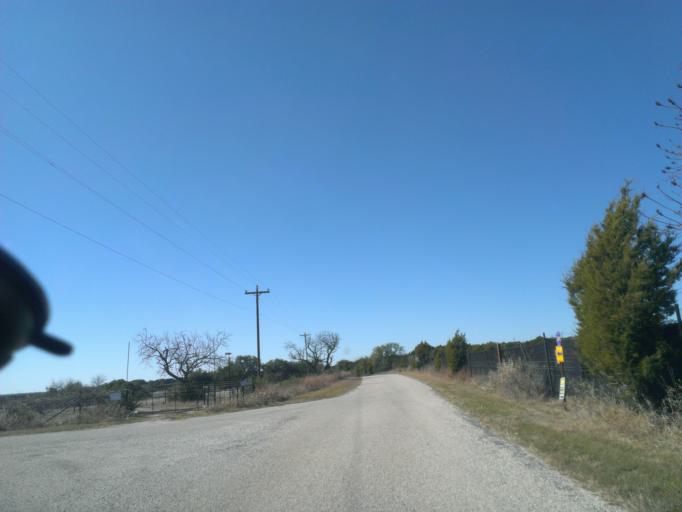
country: US
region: Texas
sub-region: Lampasas County
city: Kempner
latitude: 30.9354
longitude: -98.0265
